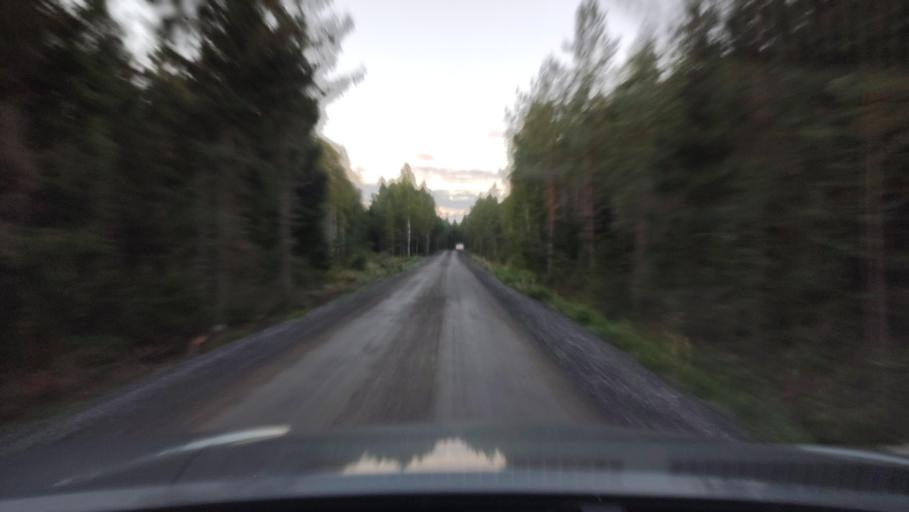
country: FI
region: Southern Ostrobothnia
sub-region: Suupohja
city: Karijoki
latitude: 62.1946
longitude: 21.5752
